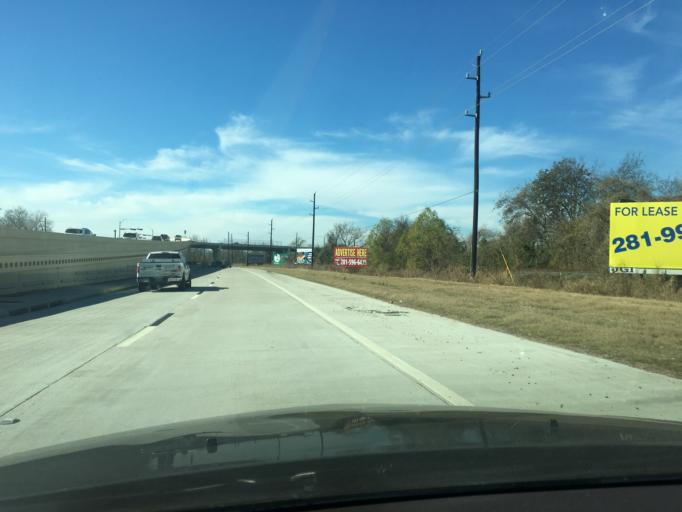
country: US
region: Texas
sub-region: Fort Bend County
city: Richmond
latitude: 29.5958
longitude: -95.7391
